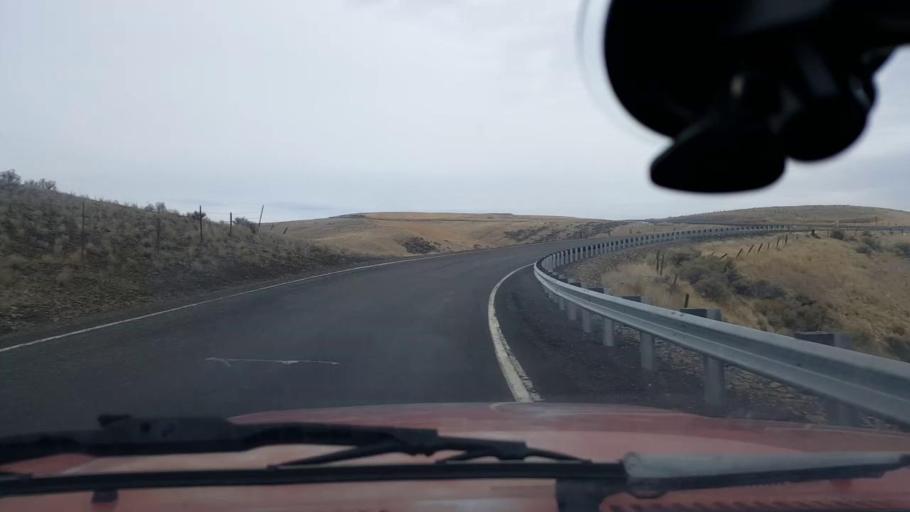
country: US
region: Washington
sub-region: Asotin County
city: Clarkston Heights-Vineland
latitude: 46.3330
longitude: -117.2968
